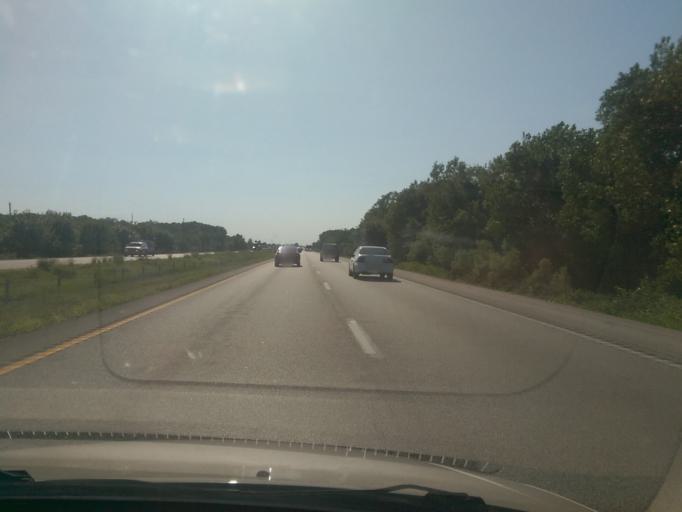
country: US
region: Missouri
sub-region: Saline County
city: Sweet Springs
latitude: 38.9775
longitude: -93.4297
